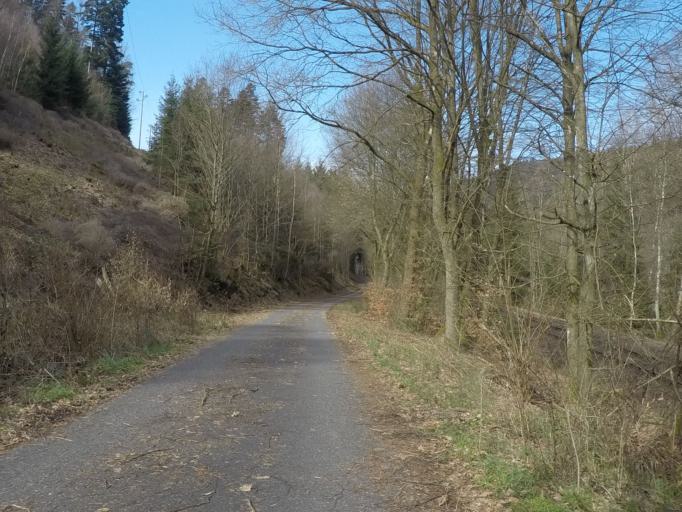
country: DE
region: Rheinland-Pfalz
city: Erfweiler
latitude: 49.2048
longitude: 7.8073
